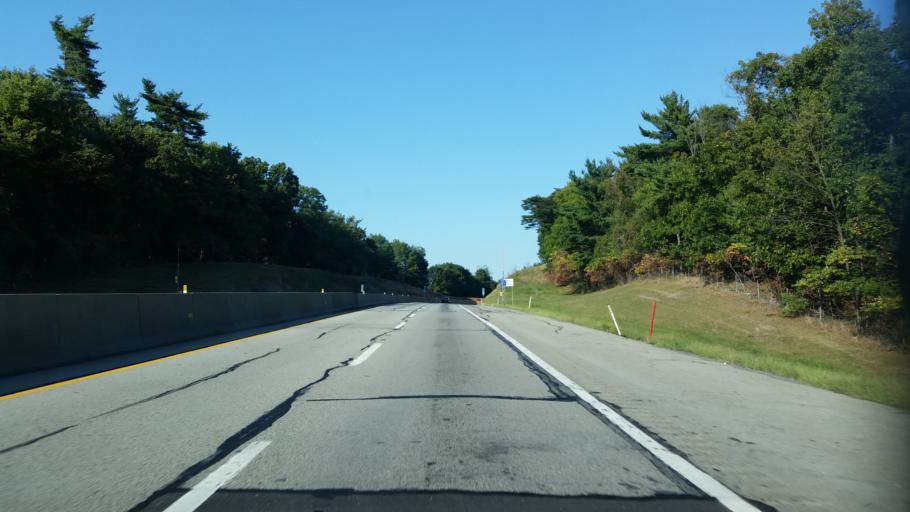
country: US
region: Pennsylvania
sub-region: Fulton County
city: McConnellsburg
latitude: 40.0561
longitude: -77.9554
